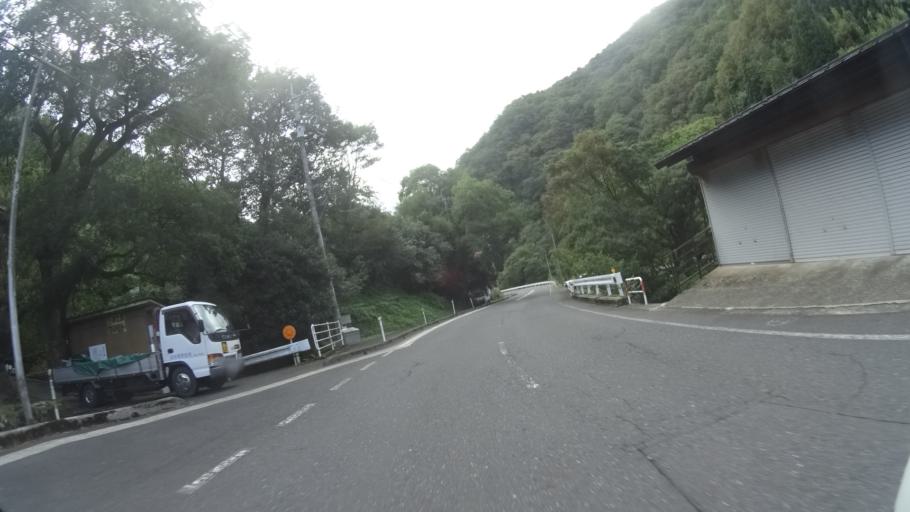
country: JP
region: Tottori
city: Kurayoshi
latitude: 35.4008
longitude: 133.9445
